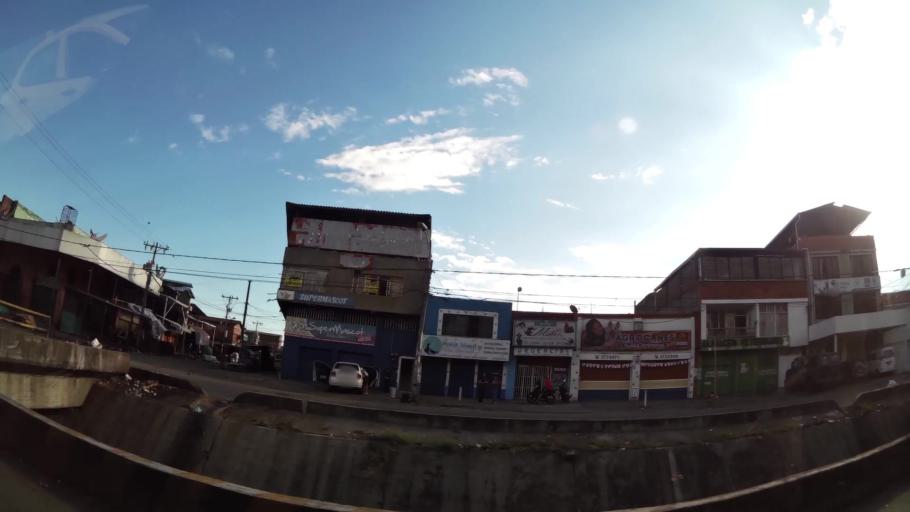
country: CO
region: Valle del Cauca
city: Cali
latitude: 3.4293
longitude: -76.5227
